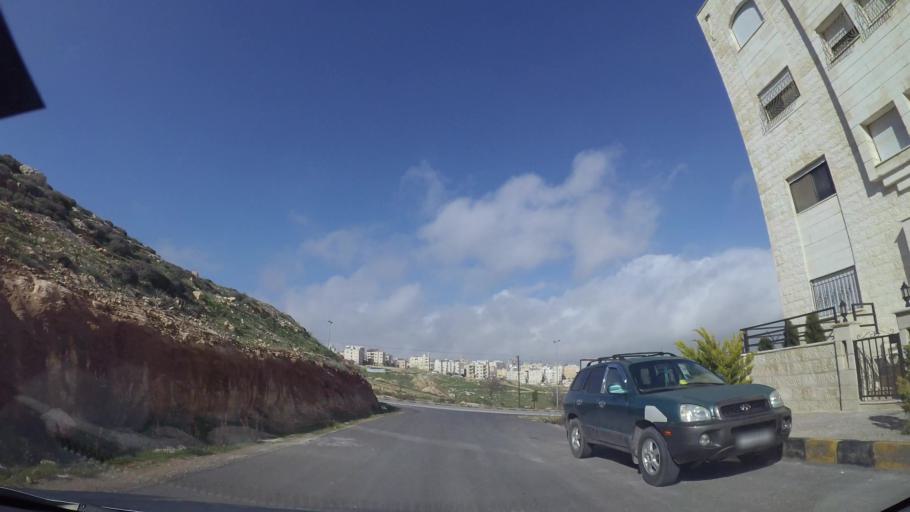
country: JO
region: Amman
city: Al Jubayhah
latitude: 32.0416
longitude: 35.8757
